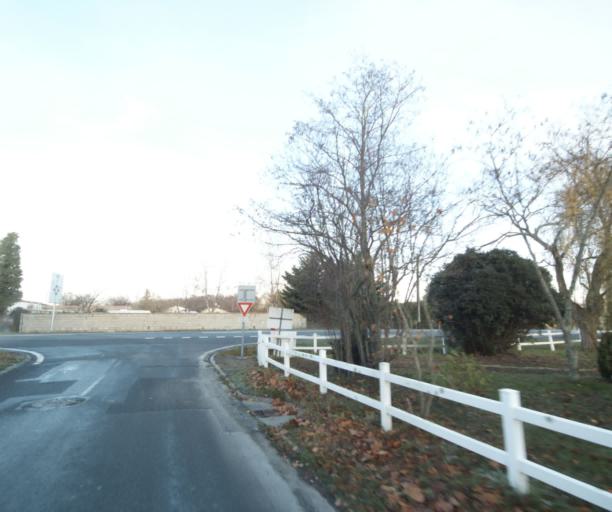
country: FR
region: Poitou-Charentes
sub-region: Departement de la Charente-Maritime
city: Fontcouverte
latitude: 45.7675
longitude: -0.5812
